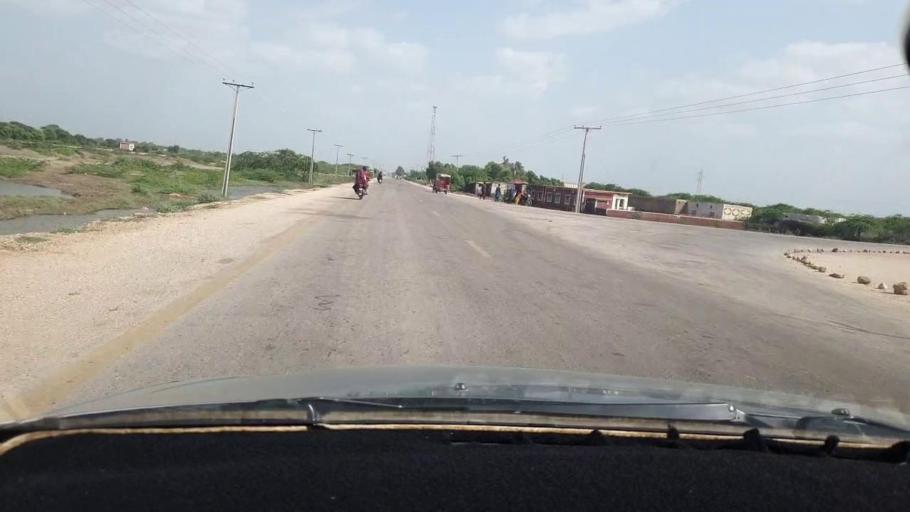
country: PK
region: Sindh
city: Naukot
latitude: 24.8671
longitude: 69.3816
